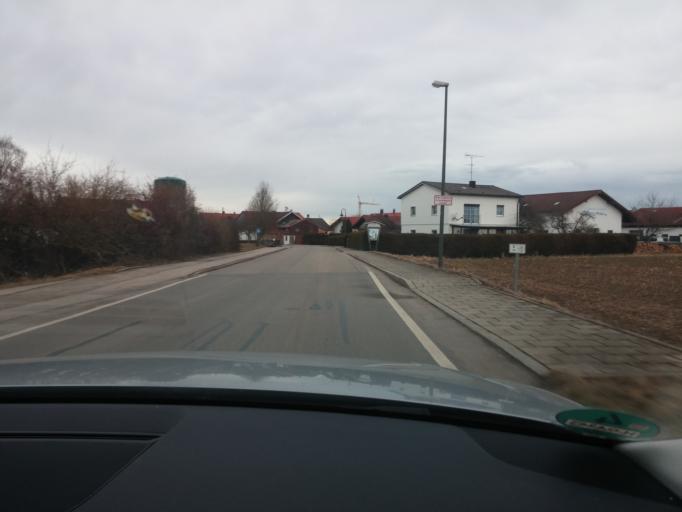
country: DE
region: Bavaria
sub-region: Upper Bavaria
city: Grasbrunn
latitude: 48.0565
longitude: 11.7715
